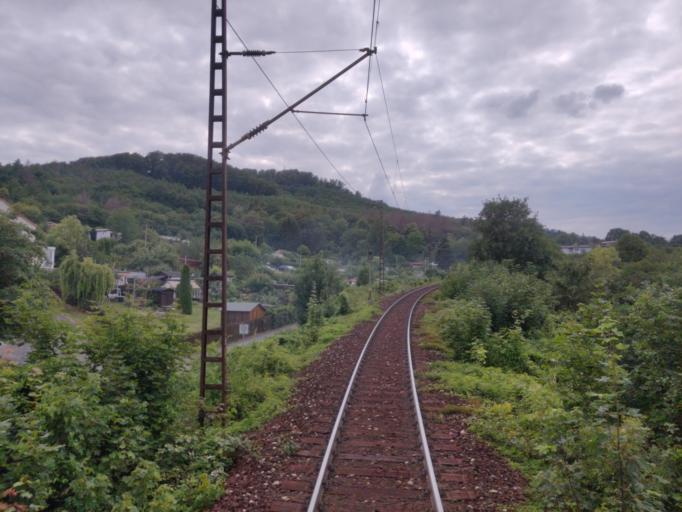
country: DE
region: Saxony-Anhalt
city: Blankenburg
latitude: 51.7953
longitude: 10.9369
